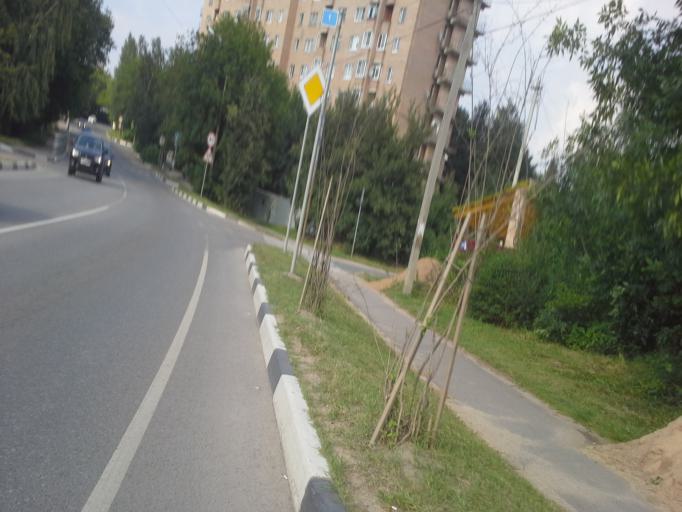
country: RU
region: Moskovskaya
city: Istra
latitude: 55.9213
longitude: 36.8727
